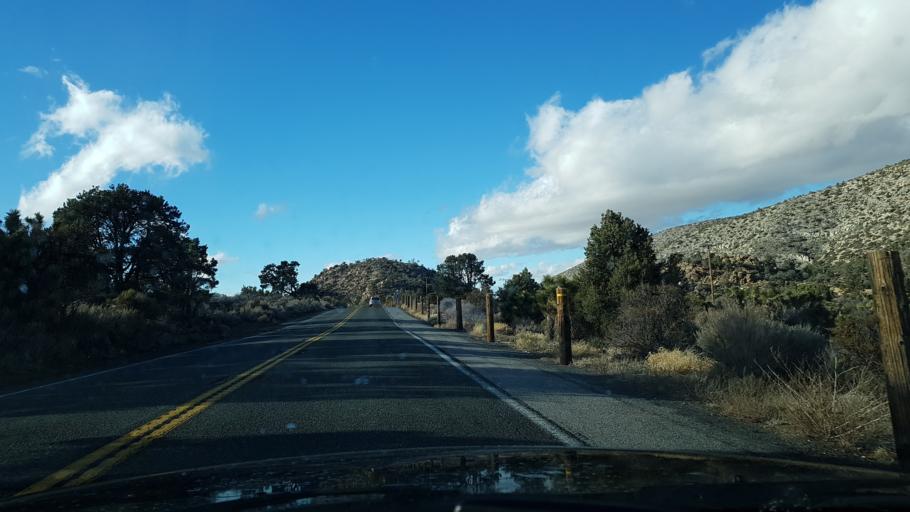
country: US
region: California
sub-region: San Bernardino County
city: Big Bear City
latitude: 34.3237
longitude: -116.8201
